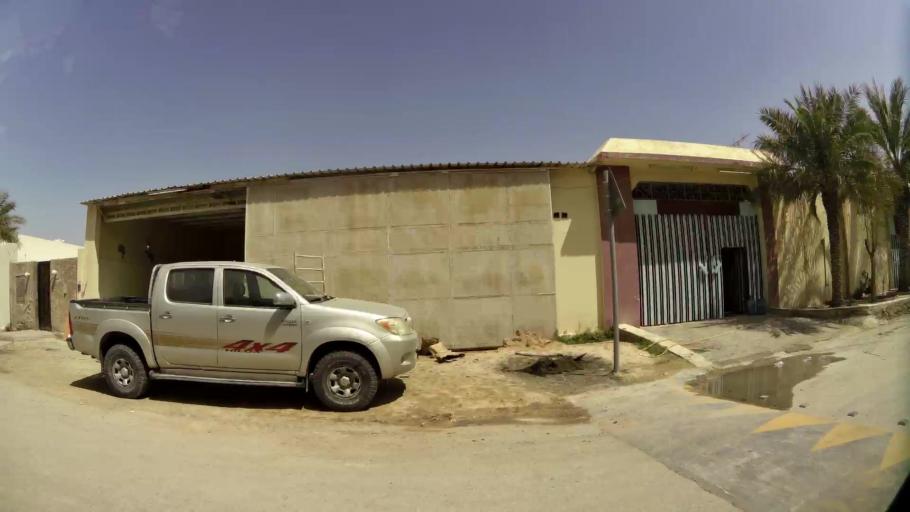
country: QA
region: Baladiyat Umm Salal
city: Umm Salal Muhammad
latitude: 25.3694
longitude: 51.4264
